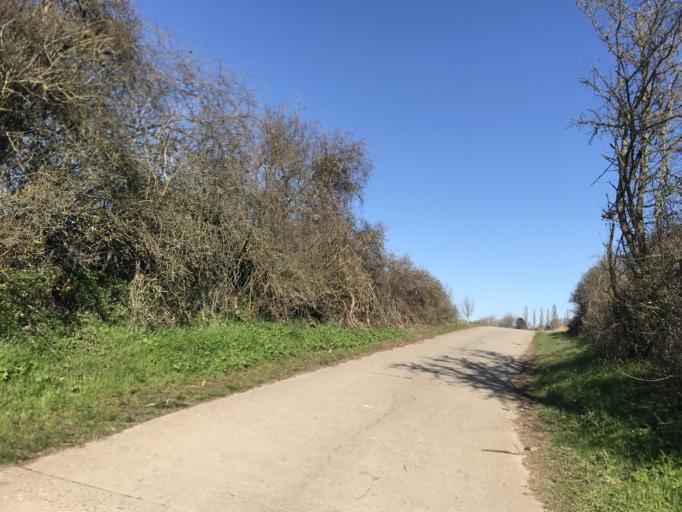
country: DE
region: Hesse
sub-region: Regierungsbezirk Darmstadt
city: Florsheim
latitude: 50.0136
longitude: 8.4048
